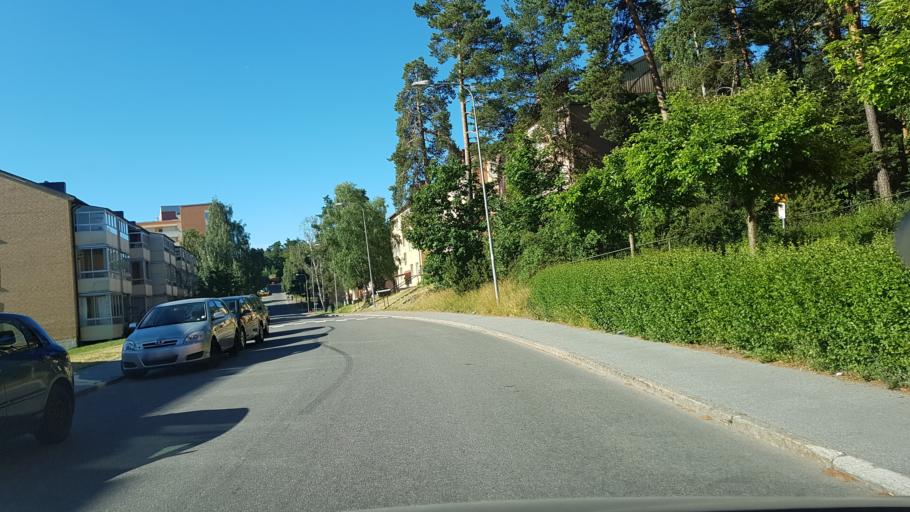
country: SE
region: Stockholm
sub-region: Jarfalla Kommun
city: Jakobsberg
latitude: 59.4200
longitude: 17.8397
